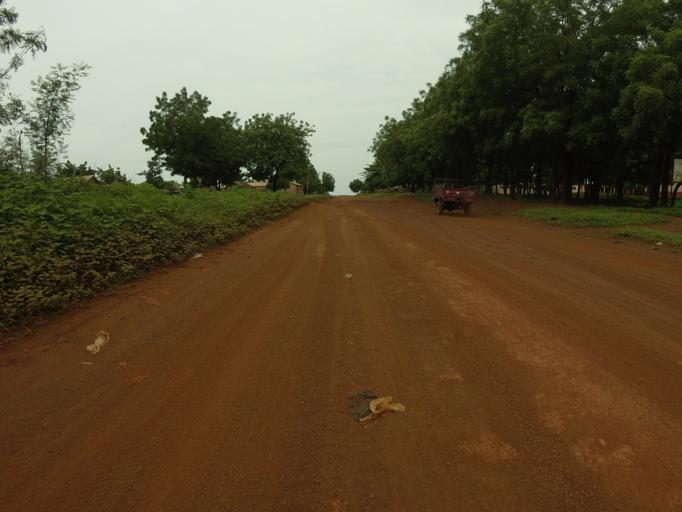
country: GH
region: Northern
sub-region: Yendi
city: Yendi
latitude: 9.0355
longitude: -0.0131
